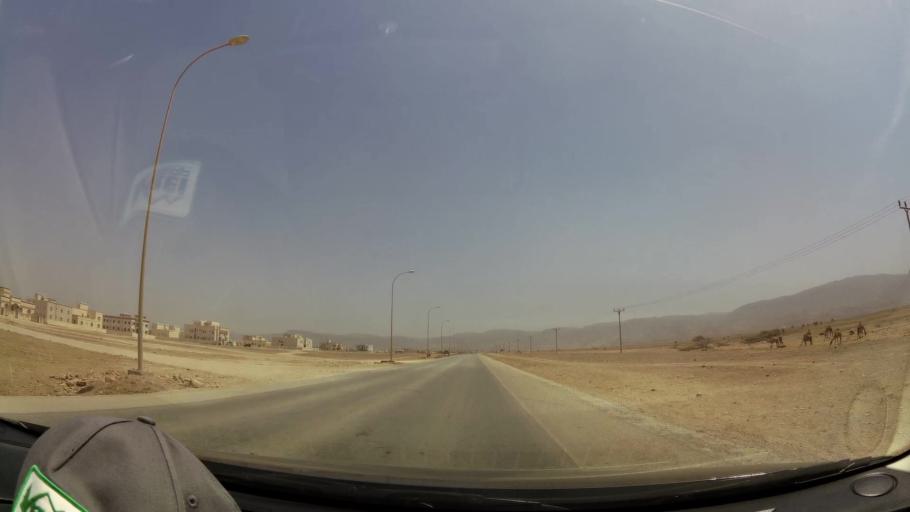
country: OM
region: Zufar
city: Salalah
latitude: 17.0825
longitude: 54.2170
